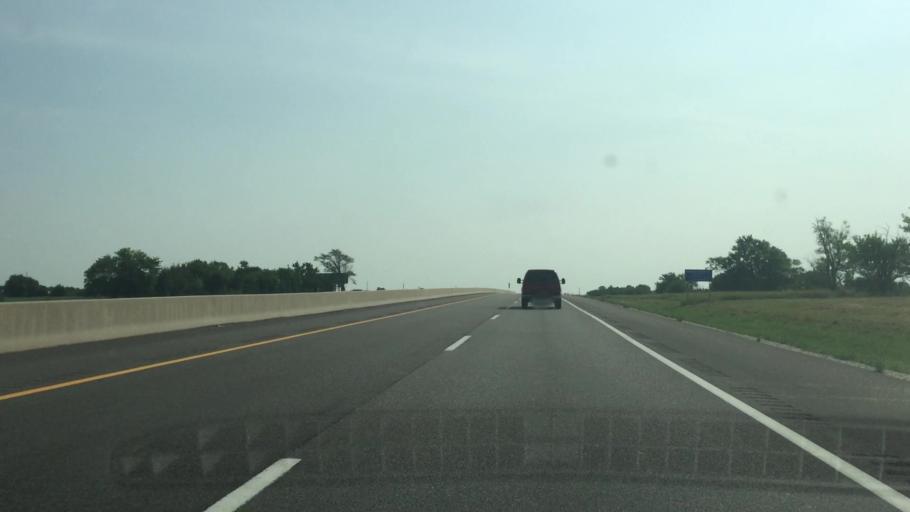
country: US
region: Kansas
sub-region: Butler County
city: Andover
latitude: 37.7405
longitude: -97.0596
